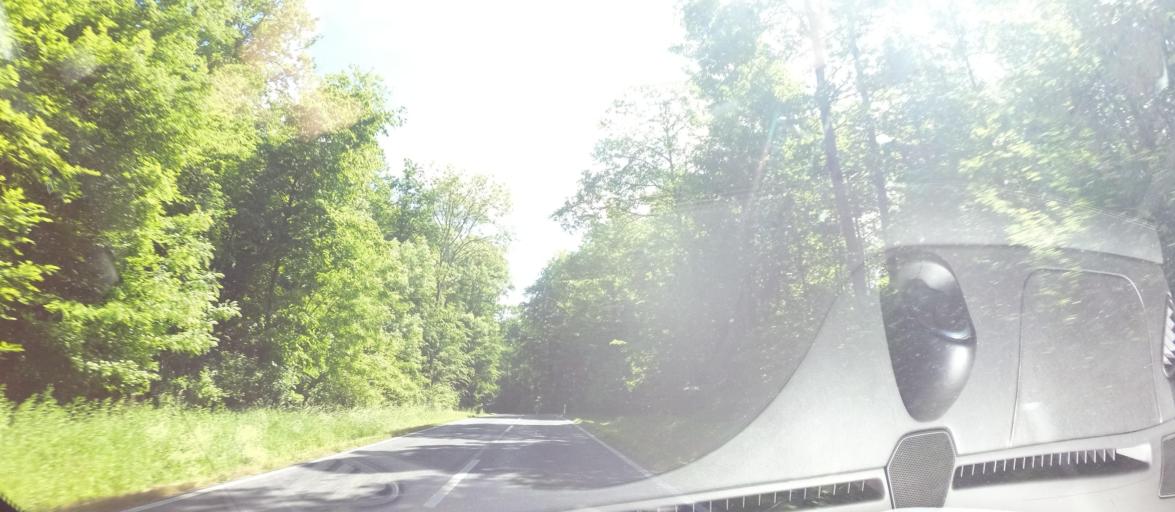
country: DE
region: Baden-Wuerttemberg
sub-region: Karlsruhe Region
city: Sinsheim
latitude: 49.1901
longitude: 8.8338
